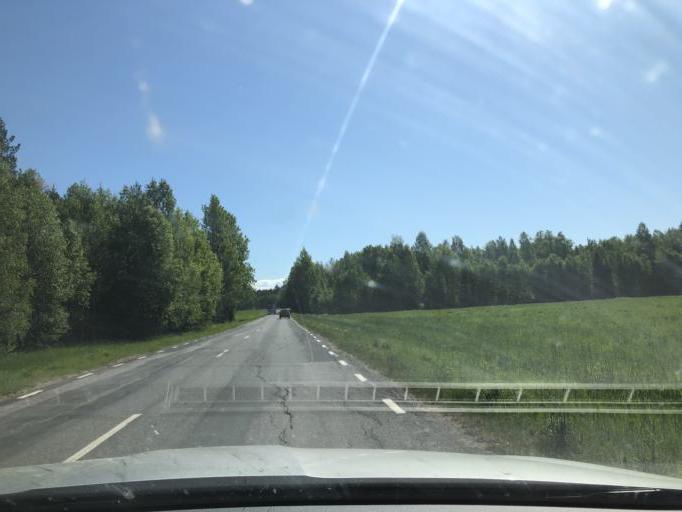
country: SE
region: Norrbotten
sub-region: Lulea Kommun
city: Gammelstad
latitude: 65.6605
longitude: 21.9838
